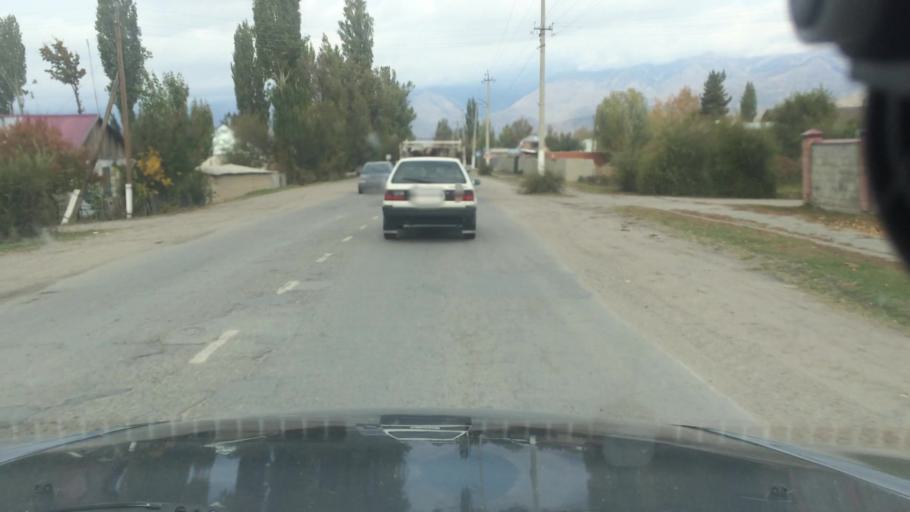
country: KG
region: Ysyk-Koel
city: Tyup
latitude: 42.7245
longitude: 78.3649
